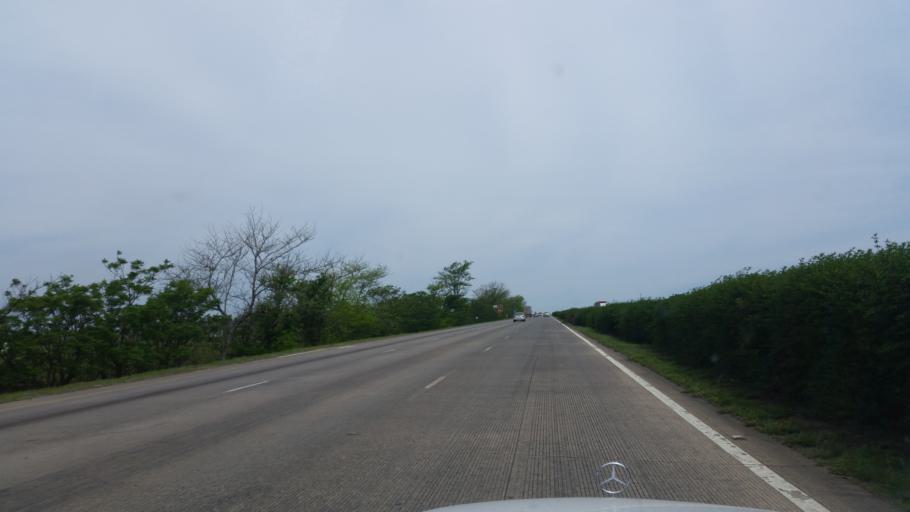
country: ZA
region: KwaZulu-Natal
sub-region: uMgungundlovu District Municipality
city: Camperdown
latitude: -29.6830
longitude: 30.4749
